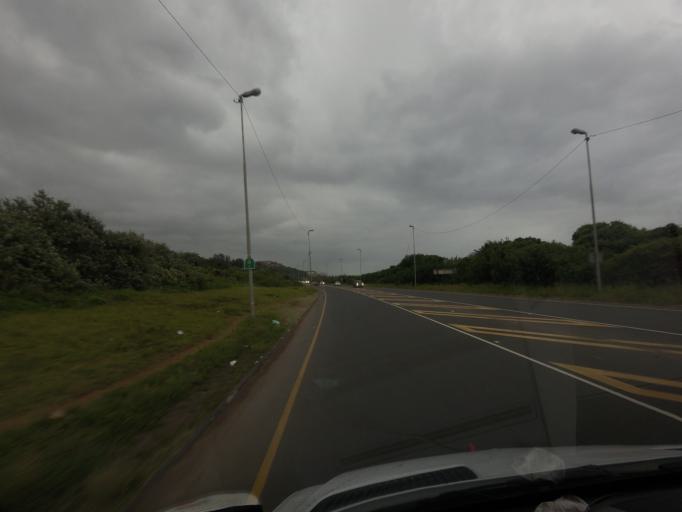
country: ZA
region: KwaZulu-Natal
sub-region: iLembe District Municipality
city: Ballitoville
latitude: -29.5962
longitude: 31.1675
